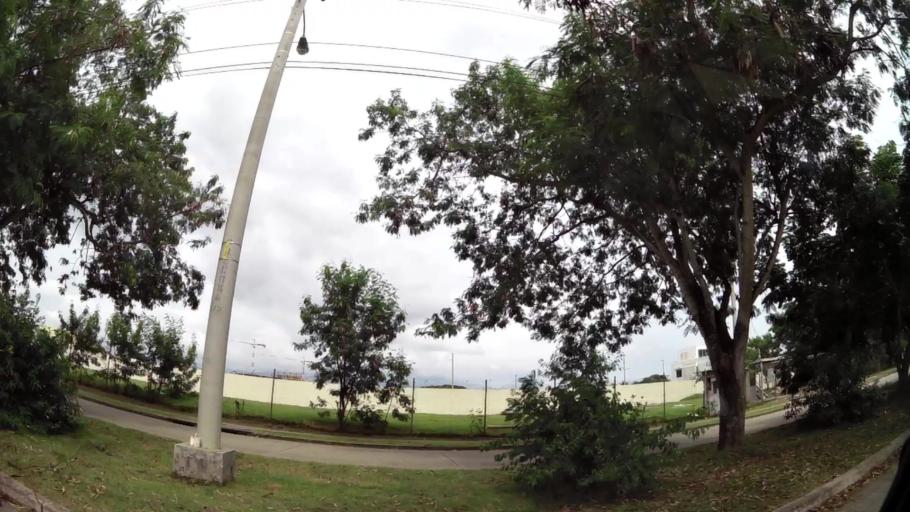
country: PA
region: Panama
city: San Miguelito
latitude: 9.0330
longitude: -79.4227
